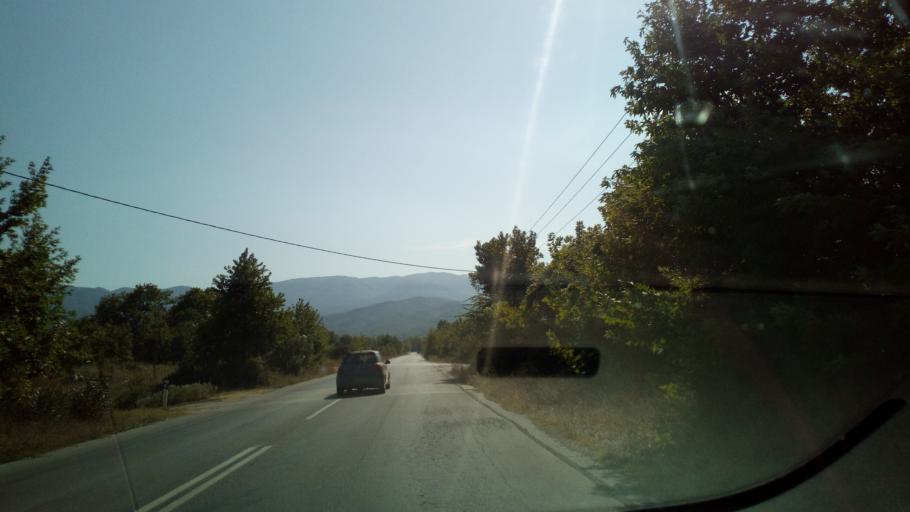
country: GR
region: Central Macedonia
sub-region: Nomos Thessalonikis
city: Stavros
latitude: 40.6056
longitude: 23.7748
